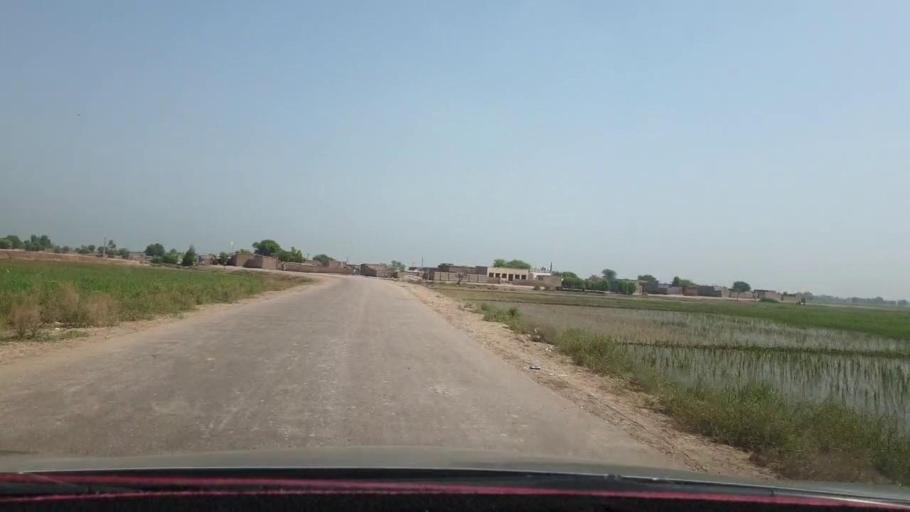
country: PK
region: Sindh
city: Warah
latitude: 27.4743
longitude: 67.8325
